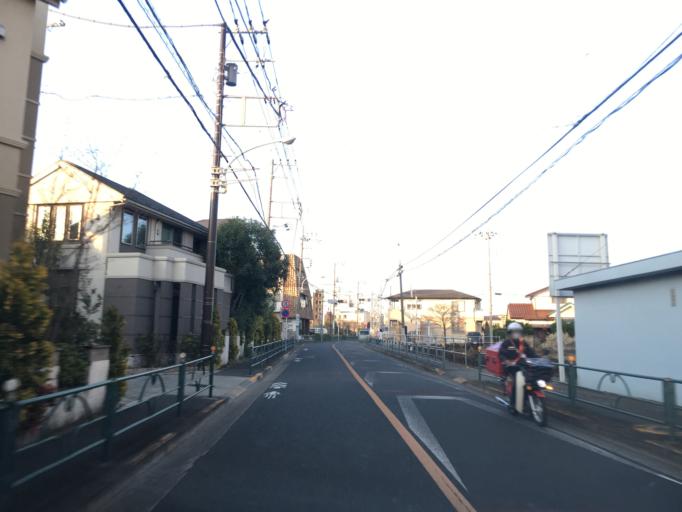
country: JP
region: Tokyo
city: Kokubunji
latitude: 35.7075
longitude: 139.4600
